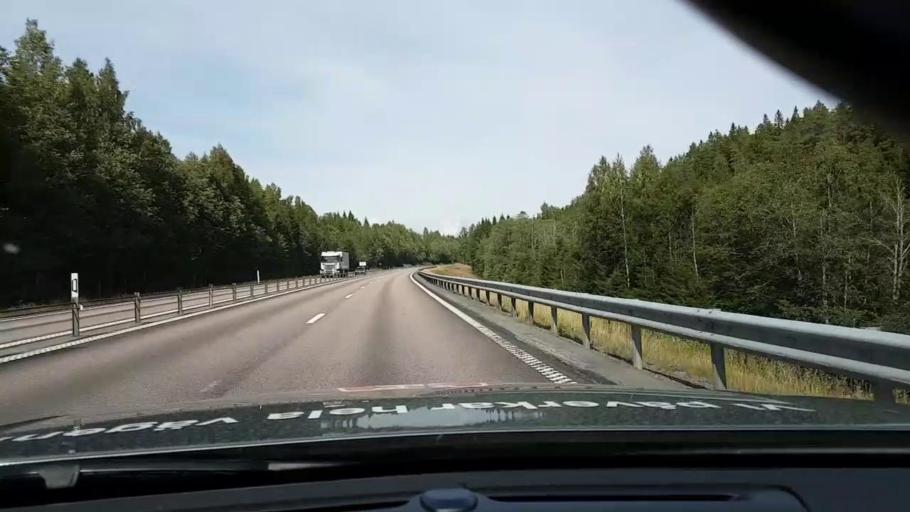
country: SE
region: Vaesternorrland
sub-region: OErnskoeldsviks Kommun
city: Husum
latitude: 63.4220
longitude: 19.2049
